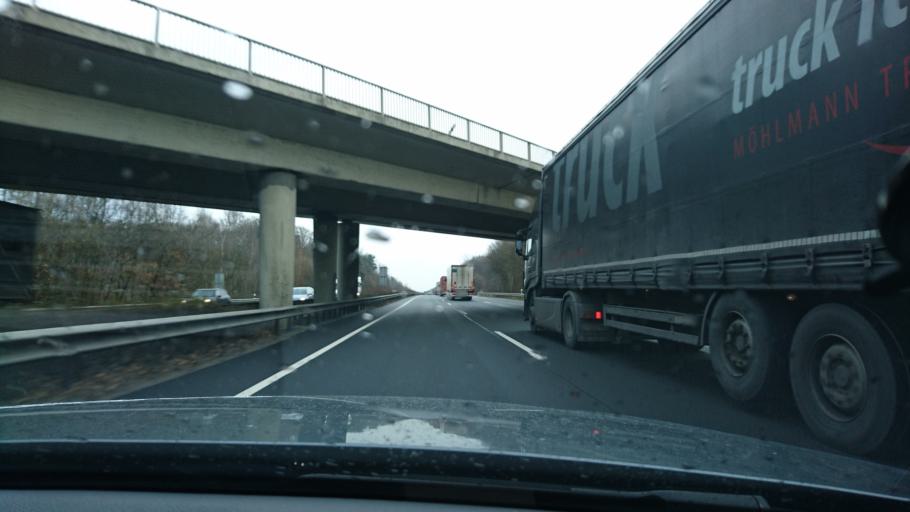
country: DE
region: Lower Saxony
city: Neuenkirchen
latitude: 52.5076
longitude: 8.0903
